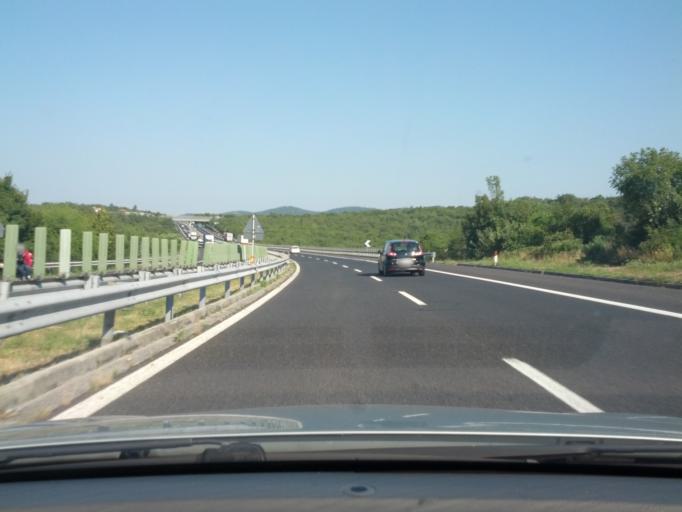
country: IT
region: Friuli Venezia Giulia
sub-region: Provincia di Trieste
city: Aurisina
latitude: 45.7596
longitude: 13.6707
